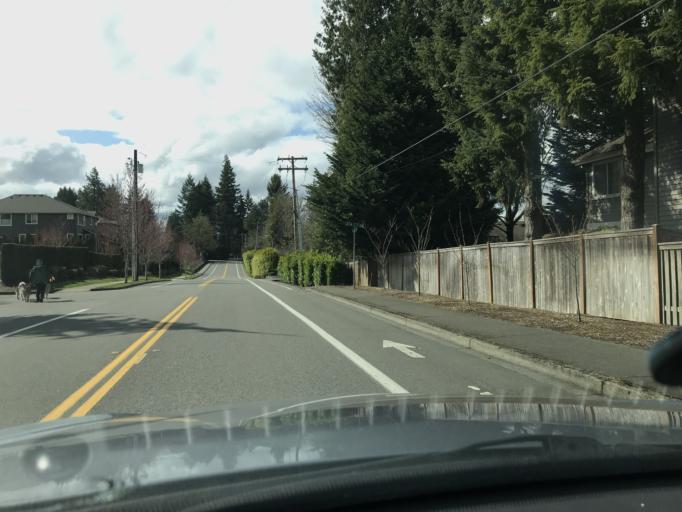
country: US
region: Washington
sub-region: King County
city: City of Sammamish
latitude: 47.5811
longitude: -122.0538
